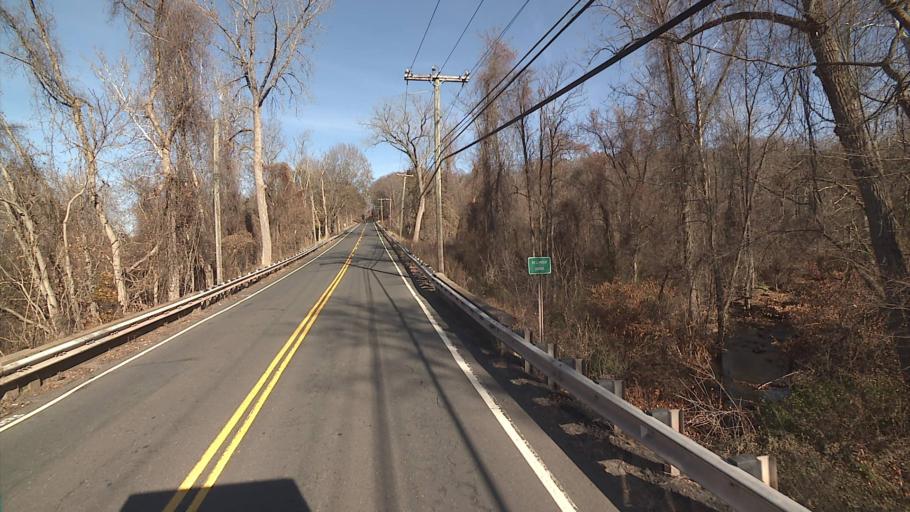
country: US
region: Connecticut
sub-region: Middlesex County
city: Cromwell
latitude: 41.6089
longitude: -72.6021
